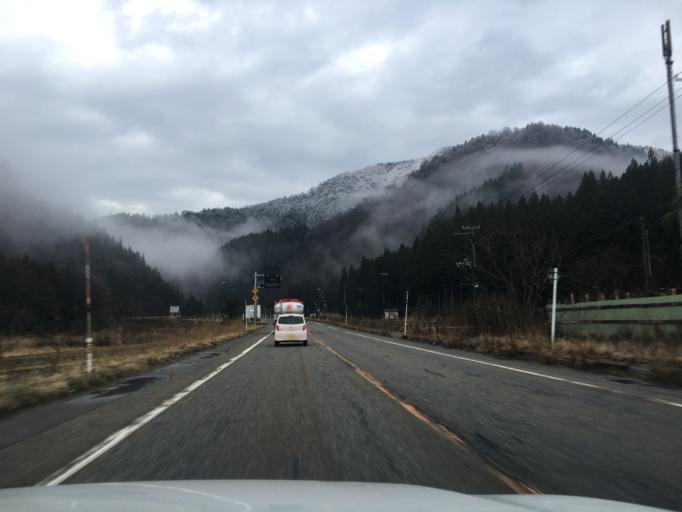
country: JP
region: Niigata
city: Murakami
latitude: 38.4602
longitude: 139.5741
